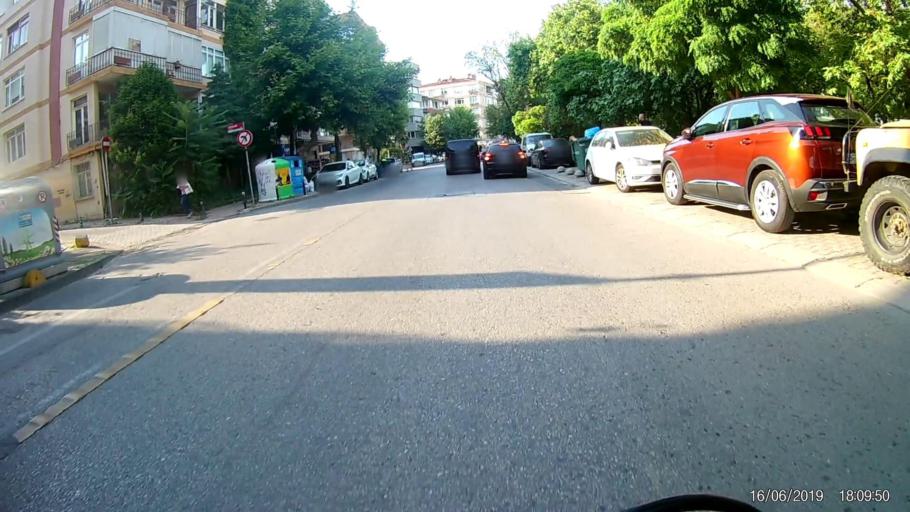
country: TR
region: Istanbul
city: UEskuedar
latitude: 40.9854
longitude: 29.0332
